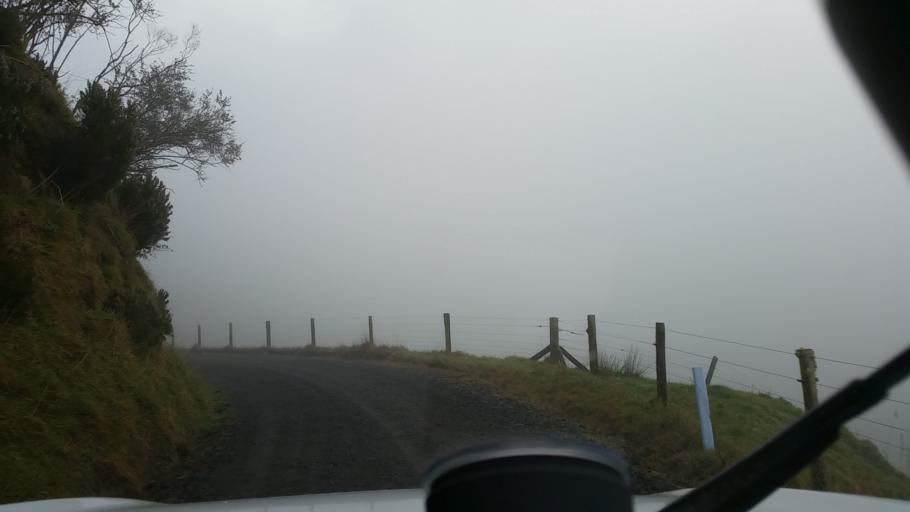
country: NZ
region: Taranaki
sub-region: South Taranaki District
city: Eltham
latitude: -39.4099
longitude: 174.4285
